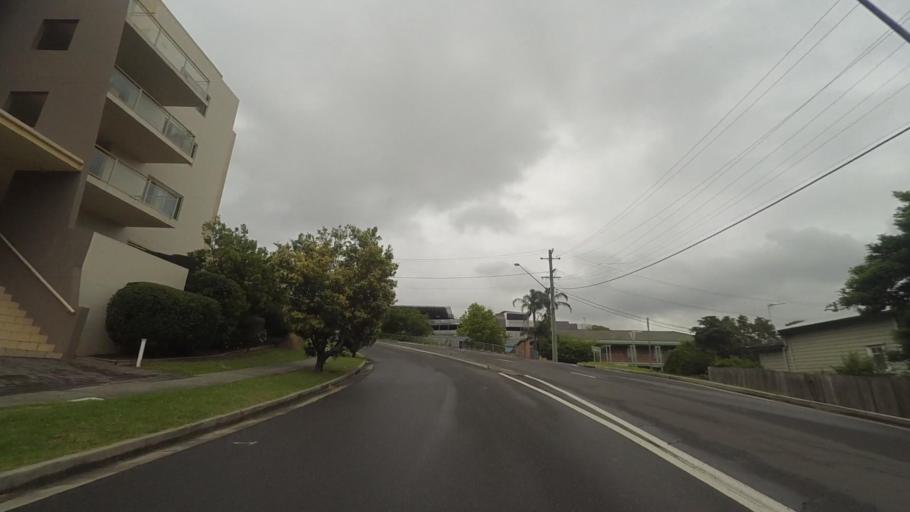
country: AU
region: New South Wales
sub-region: Wollongong
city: Gwynneville
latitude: -34.4230
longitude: 150.8825
